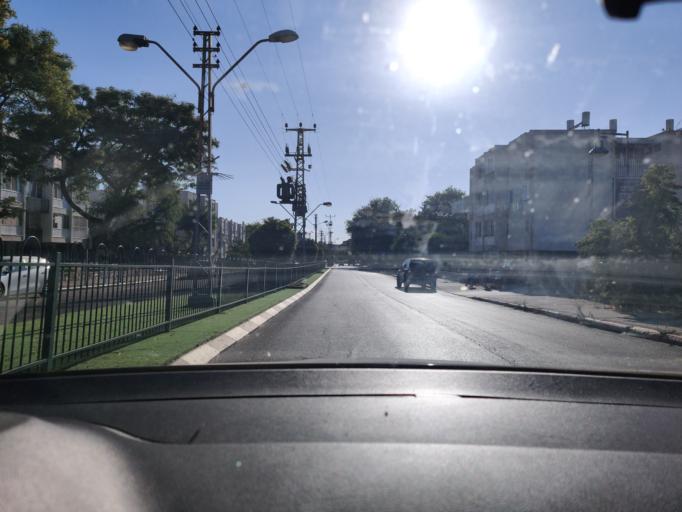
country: IL
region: Haifa
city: Hadera
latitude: 32.4721
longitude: 34.9562
